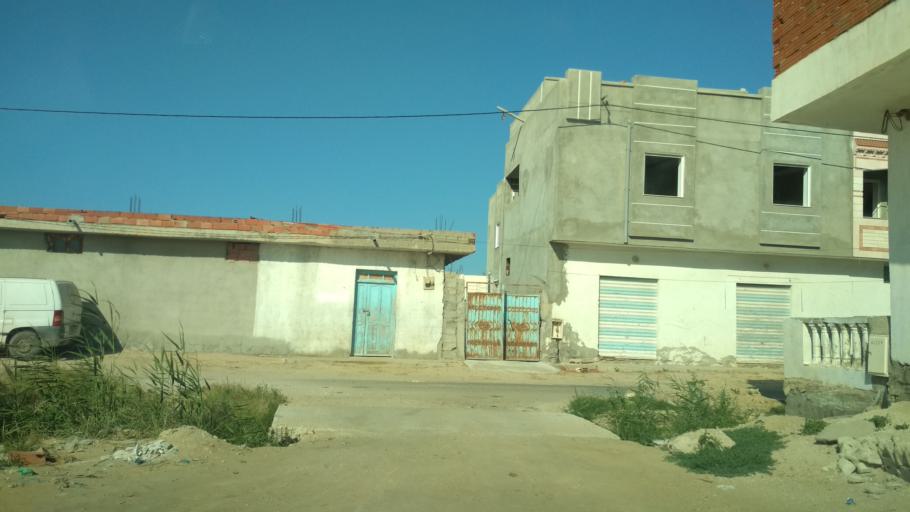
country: TN
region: Qabis
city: Gabes
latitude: 33.9478
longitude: 10.0608
